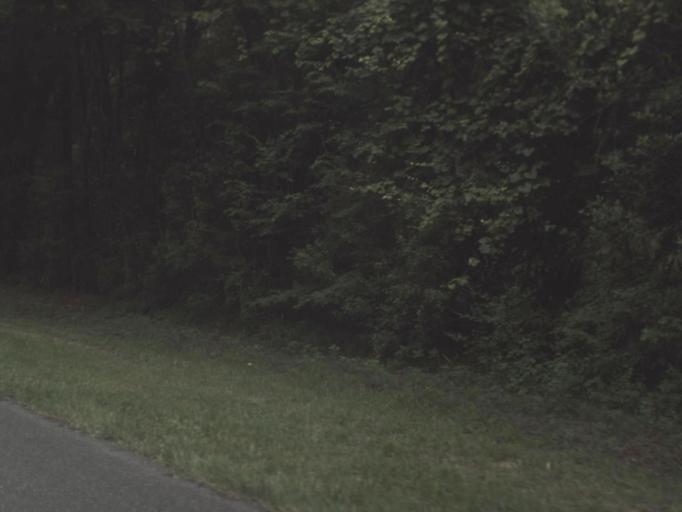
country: US
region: Florida
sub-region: Alachua County
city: Newberry
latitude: 29.5996
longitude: -82.5731
